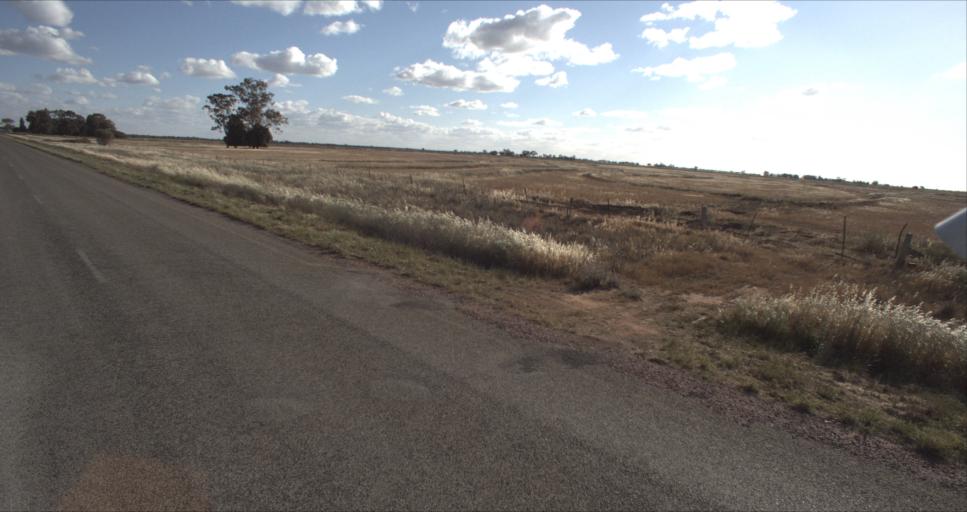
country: AU
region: New South Wales
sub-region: Leeton
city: Leeton
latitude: -34.5339
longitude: 146.2809
